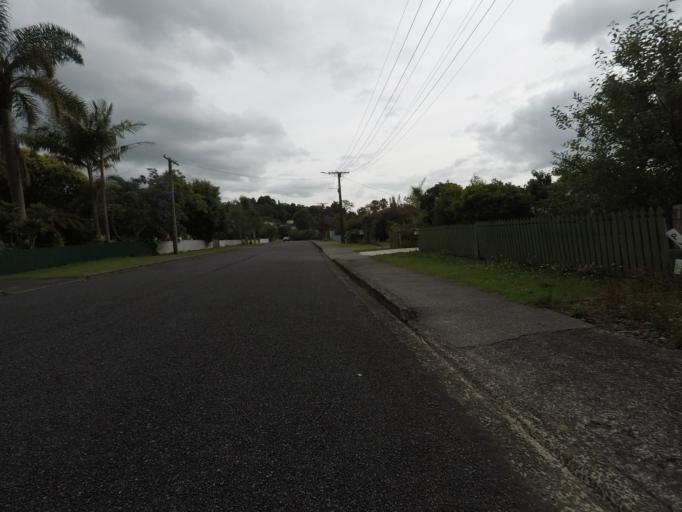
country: NZ
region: Northland
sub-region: Whangarei
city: Whangarei
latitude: -35.7174
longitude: 174.3281
